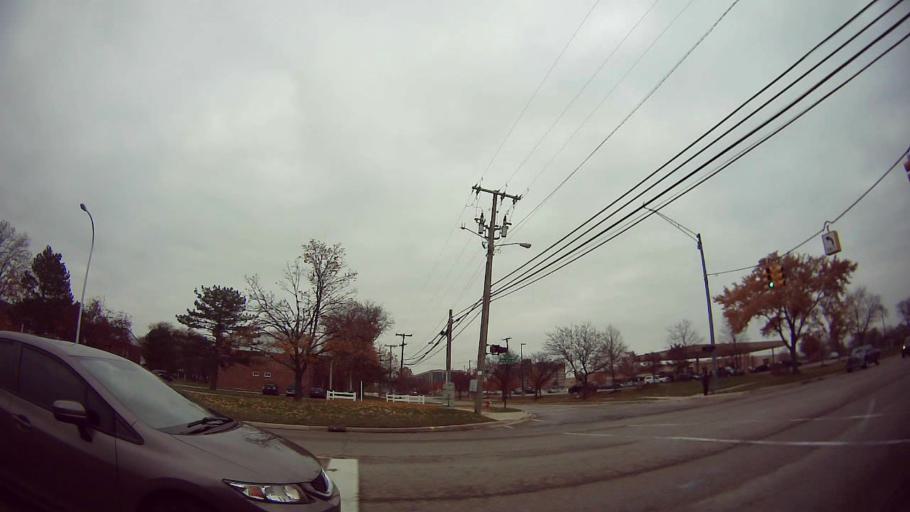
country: US
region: Michigan
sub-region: Oakland County
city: Madison Heights
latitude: 42.5226
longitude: -83.1066
